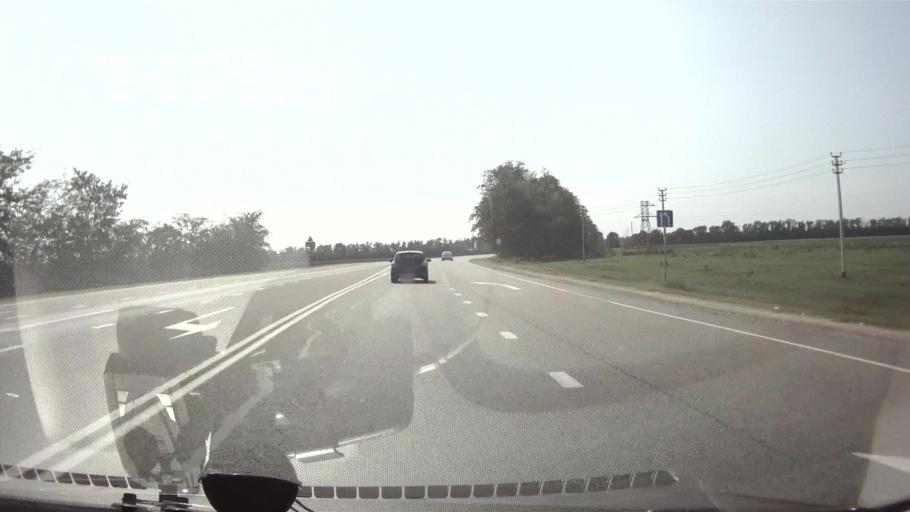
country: RU
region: Krasnodarskiy
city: Vasyurinskaya
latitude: 45.0952
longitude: 39.3841
